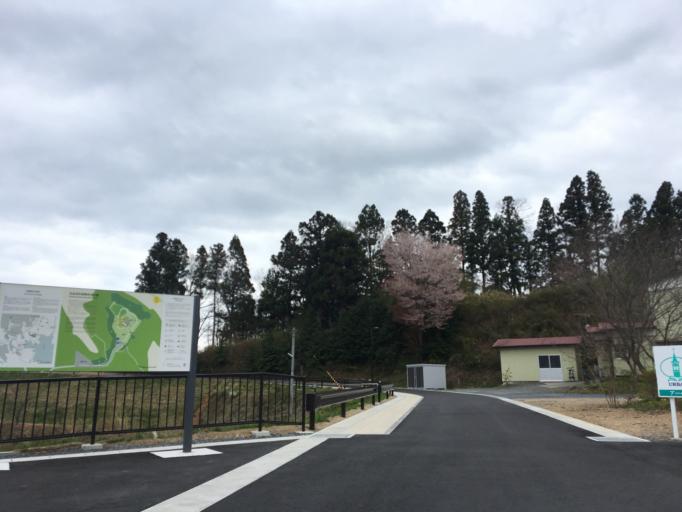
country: JP
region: Iwate
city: Ofunato
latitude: 38.9101
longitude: 141.5768
